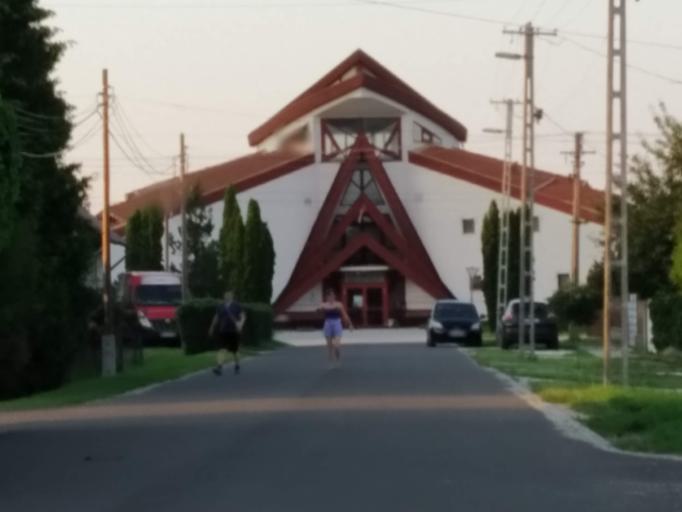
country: HU
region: Komarom-Esztergom
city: Tat
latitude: 47.7390
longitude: 18.6469
